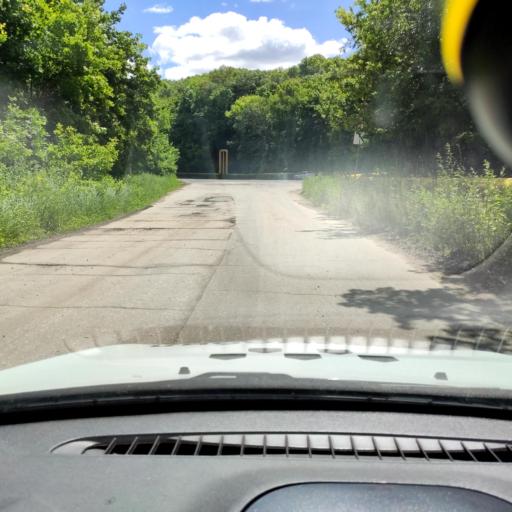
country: RU
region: Samara
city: Zhigulevsk
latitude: 53.3976
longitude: 49.4127
